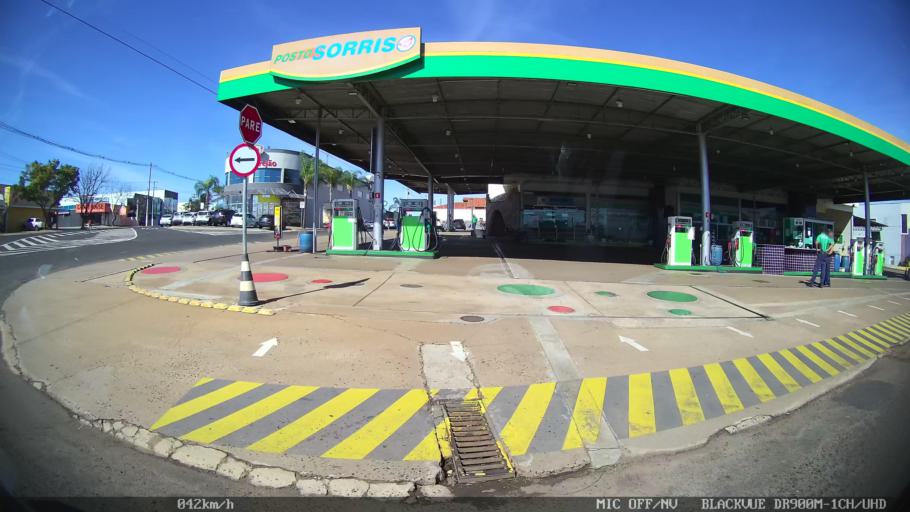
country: BR
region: Sao Paulo
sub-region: Franca
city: Franca
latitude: -20.5424
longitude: -47.3758
